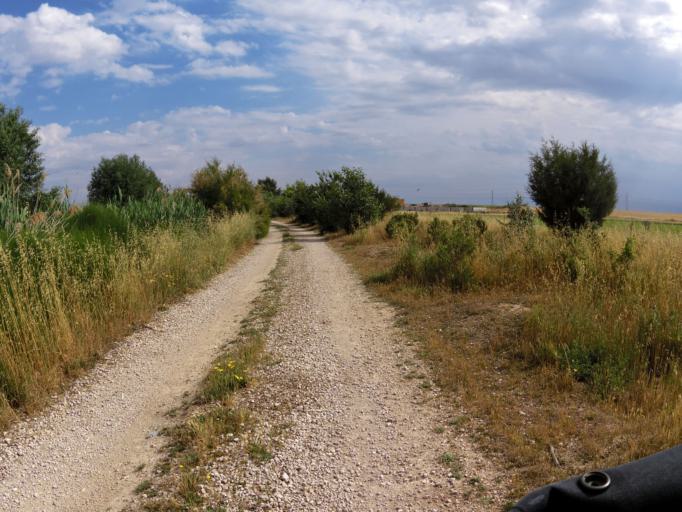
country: ES
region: Castille-La Mancha
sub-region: Provincia de Albacete
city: Albacete
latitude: 39.0270
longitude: -1.7919
